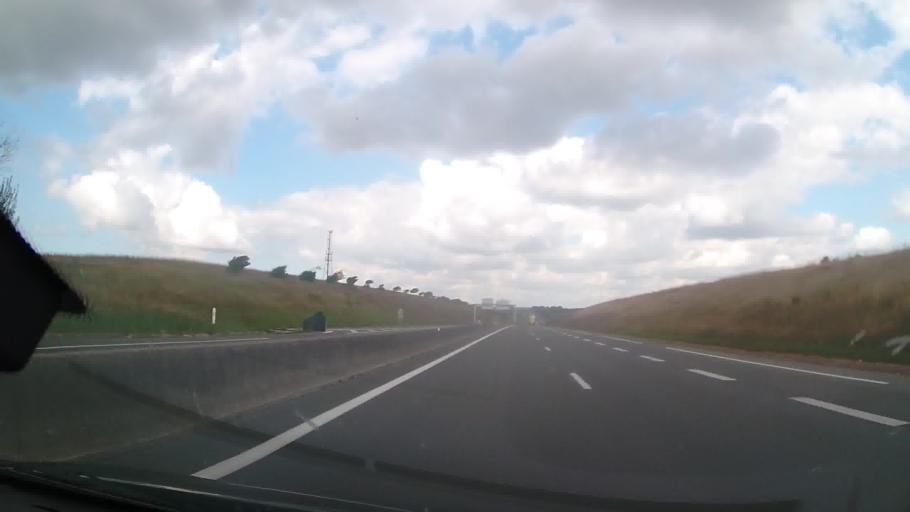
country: FR
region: Nord-Pas-de-Calais
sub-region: Departement du Pas-de-Calais
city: Verton
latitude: 50.4092
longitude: 1.6933
